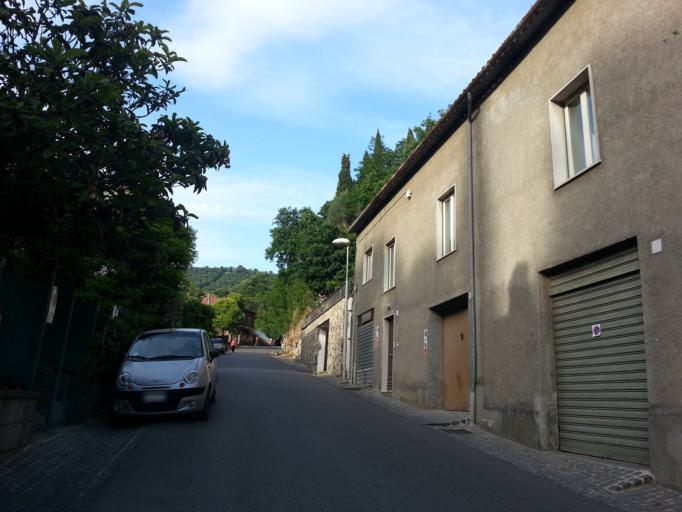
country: IT
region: Latium
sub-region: Provincia di Viterbo
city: Bolsena
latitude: 42.6447
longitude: 11.9901
